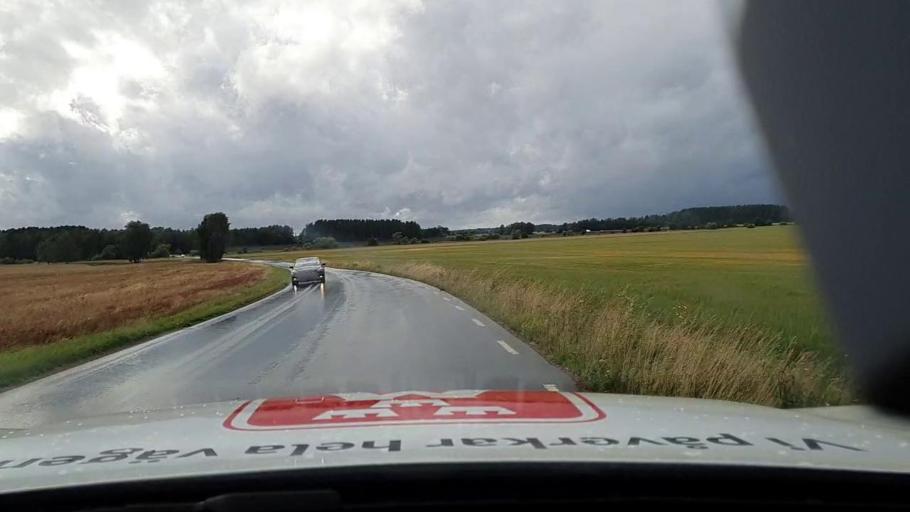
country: SE
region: Vaestra Goetaland
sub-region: Skovde Kommun
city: Stopen
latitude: 58.5291
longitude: 13.9193
